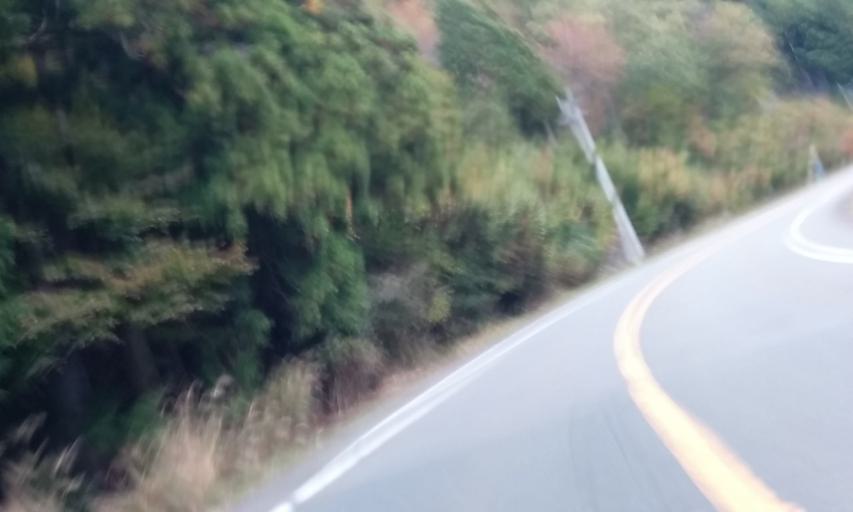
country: JP
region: Fukui
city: Obama
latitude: 35.3413
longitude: 135.5851
